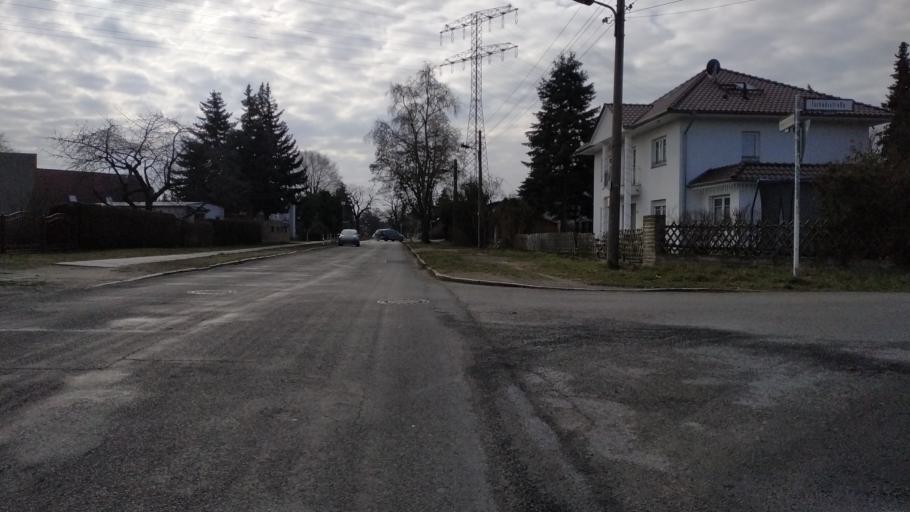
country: DE
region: Berlin
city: Hellersdorf
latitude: 52.5255
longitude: 13.6062
